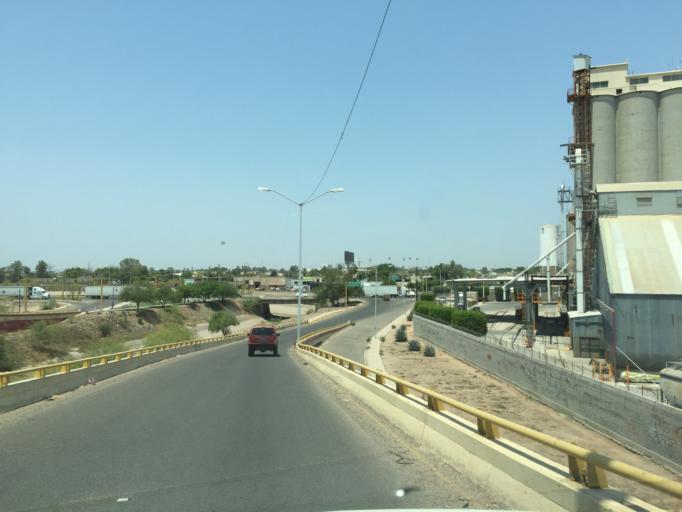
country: MX
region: Sonora
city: Navojoa
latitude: 27.0667
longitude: -109.4402
